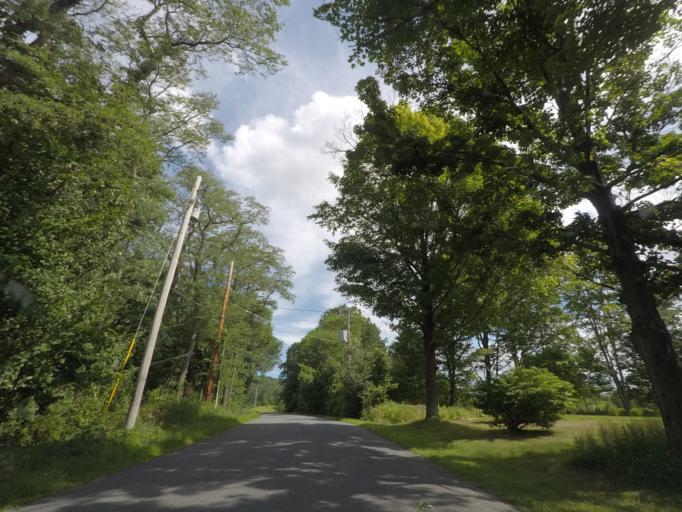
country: US
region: New York
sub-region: Rensselaer County
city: Poestenkill
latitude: 42.6872
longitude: -73.5607
